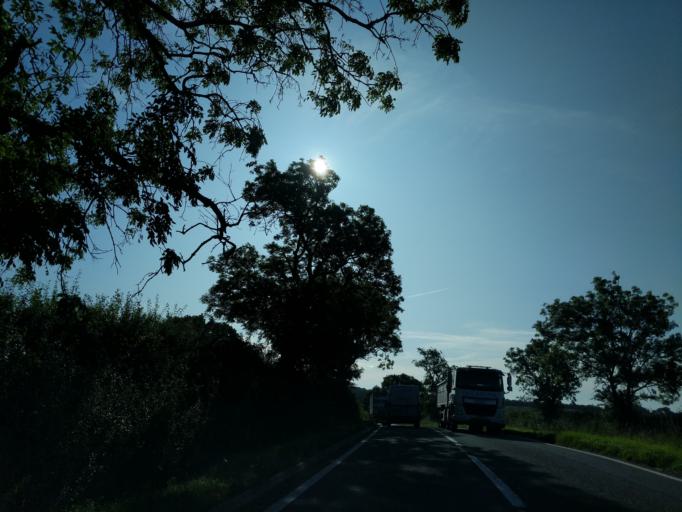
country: GB
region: England
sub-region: District of Rutland
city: Clipsham
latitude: 52.7997
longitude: -0.5710
